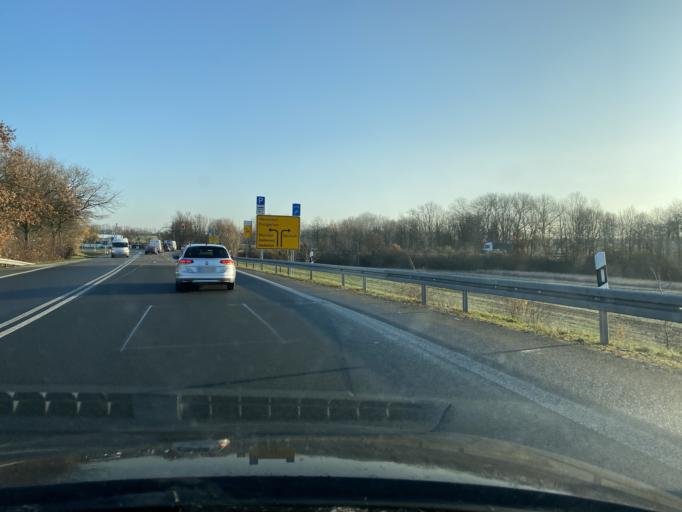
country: DE
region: North Rhine-Westphalia
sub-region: Regierungsbezirk Munster
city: Beckum
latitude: 51.7778
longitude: 8.0312
